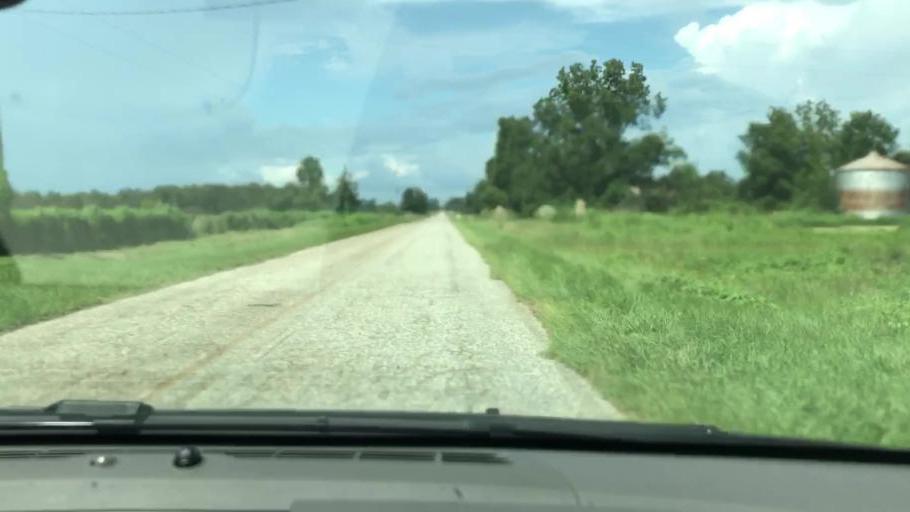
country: US
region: Georgia
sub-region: Seminole County
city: Donalsonville
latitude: 31.1910
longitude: -85.0040
